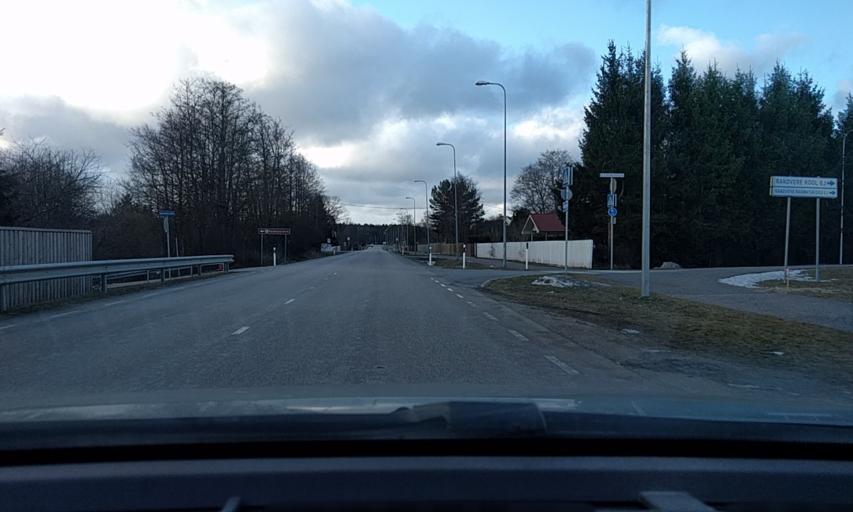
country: EE
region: Harju
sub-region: Viimsi vald
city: Viimsi
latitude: 59.5038
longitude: 24.9048
